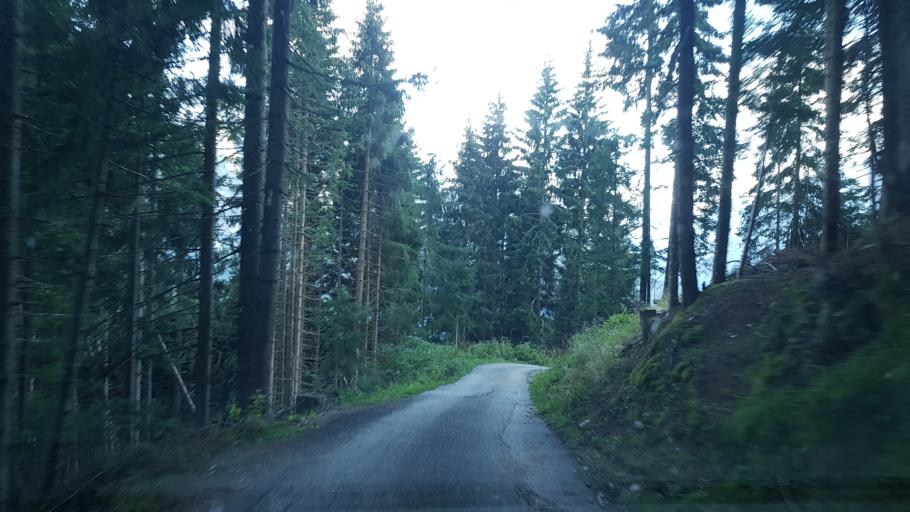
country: IT
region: Veneto
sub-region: Provincia di Belluno
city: San Pietro di Cadore
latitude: 46.5915
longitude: 12.5921
